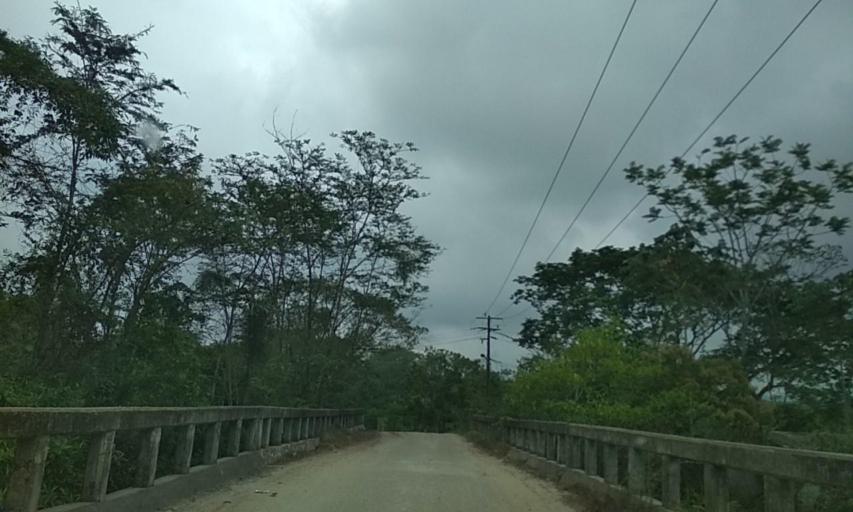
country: MX
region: Tabasco
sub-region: Huimanguillo
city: Francisco Rueda
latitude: 17.4421
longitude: -94.0672
